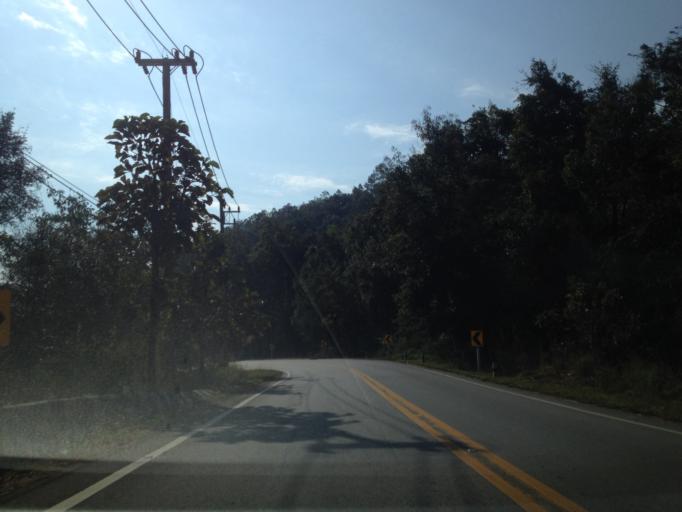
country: TH
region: Mae Hong Son
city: Pa Pae
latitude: 18.1532
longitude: 98.2421
